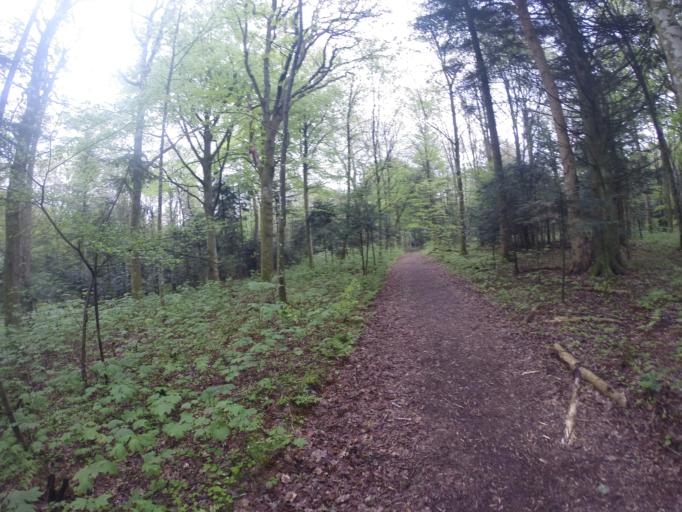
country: DK
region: North Denmark
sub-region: Thisted Kommune
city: Hanstholm
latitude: 57.0307
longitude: 8.5912
